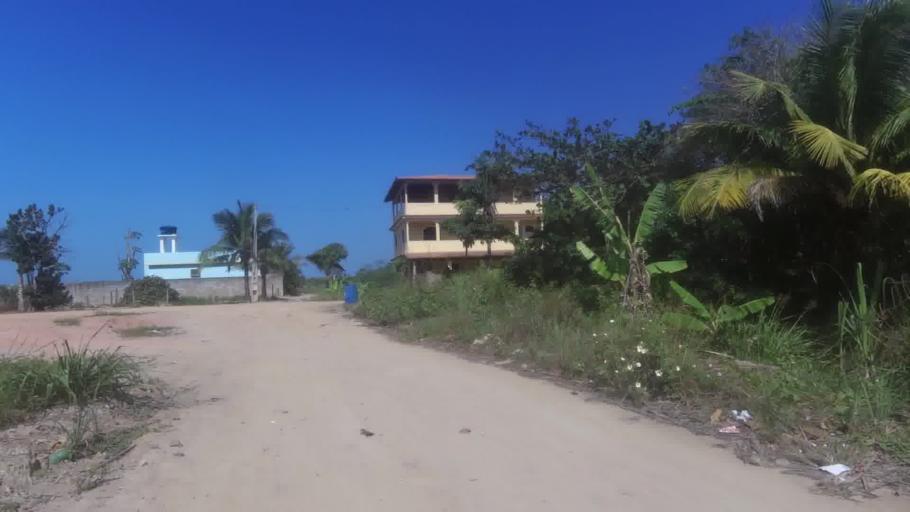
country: BR
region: Espirito Santo
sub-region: Marataizes
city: Marataizes
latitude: -21.0933
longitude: -40.8461
